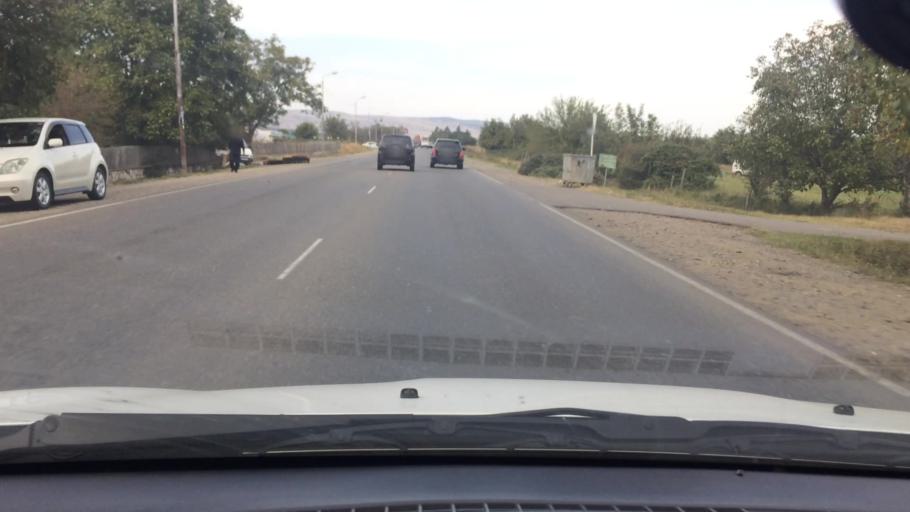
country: GE
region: Kvemo Kartli
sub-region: Marneuli
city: Marneuli
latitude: 41.5857
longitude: 44.7788
